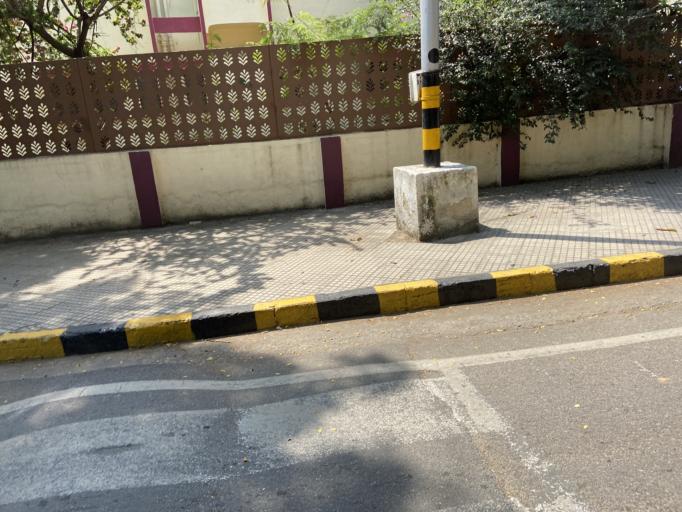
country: IN
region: Karnataka
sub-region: Bangalore Urban
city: Bangalore
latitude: 12.9841
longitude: 77.6608
